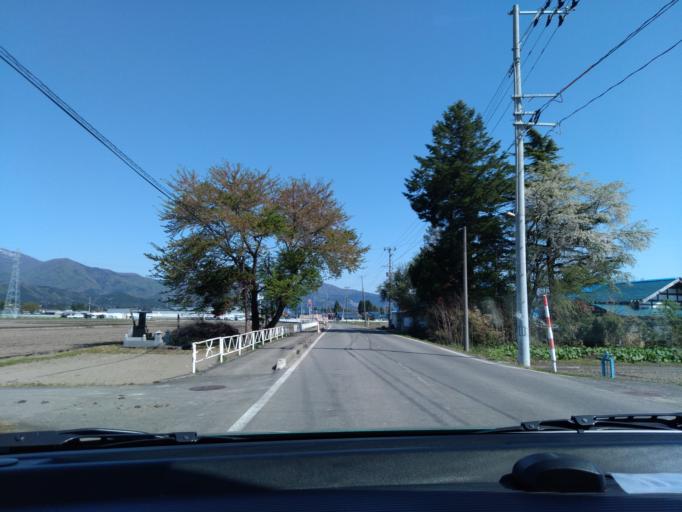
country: JP
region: Akita
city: Kakunodatemachi
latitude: 39.5731
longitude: 140.5764
